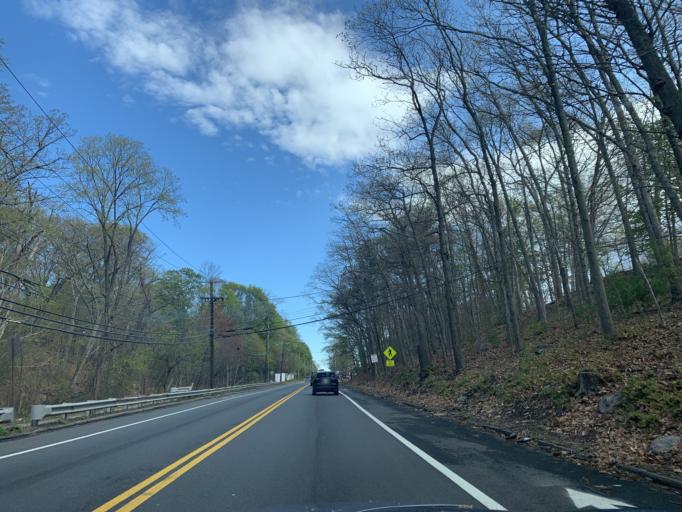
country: US
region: Massachusetts
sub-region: Norfolk County
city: Dedham
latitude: 42.2152
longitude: -71.1198
